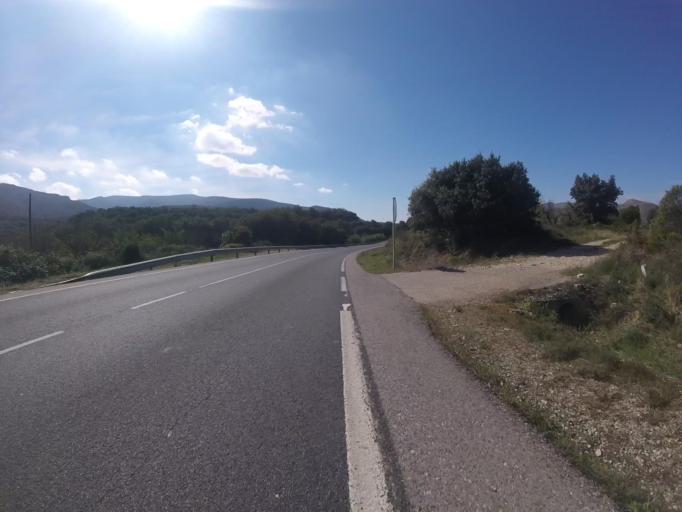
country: ES
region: Valencia
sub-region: Provincia de Castello
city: Sarratella
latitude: 40.3331
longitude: -0.0137
